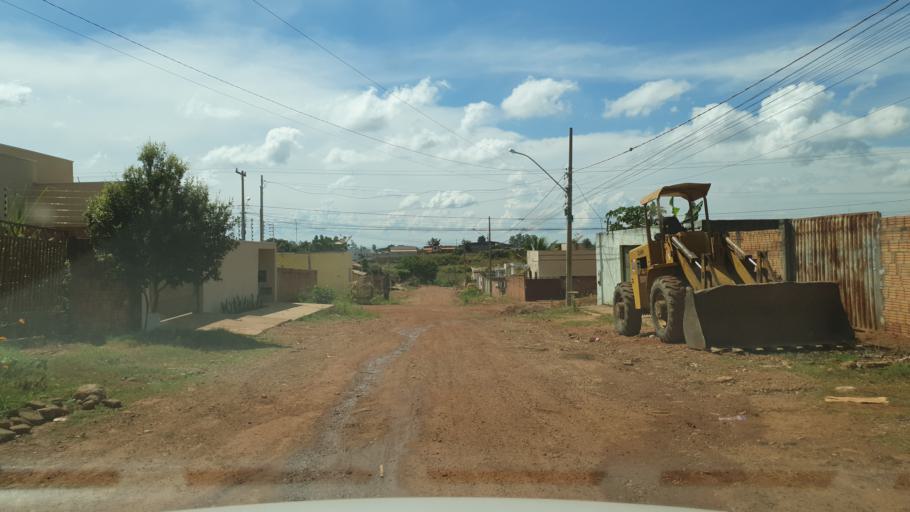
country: BR
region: Mato Grosso
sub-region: Pontes E Lacerda
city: Pontes e Lacerda
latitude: -15.2522
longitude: -59.3153
